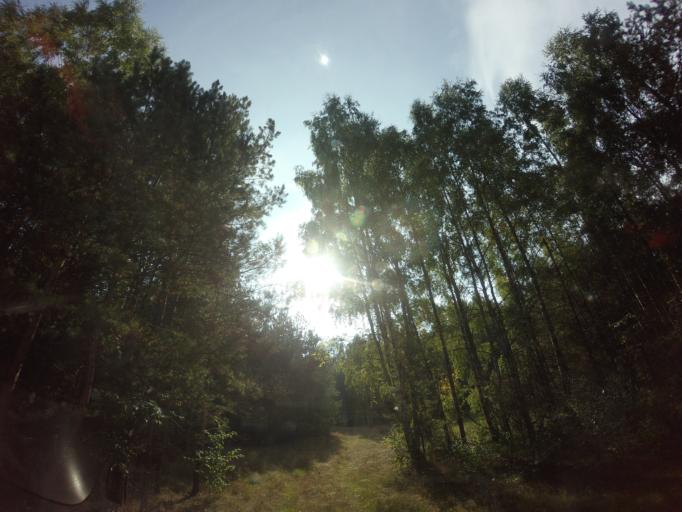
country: PL
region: West Pomeranian Voivodeship
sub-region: Powiat drawski
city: Drawsko Pomorskie
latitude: 53.4574
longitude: 15.7292
